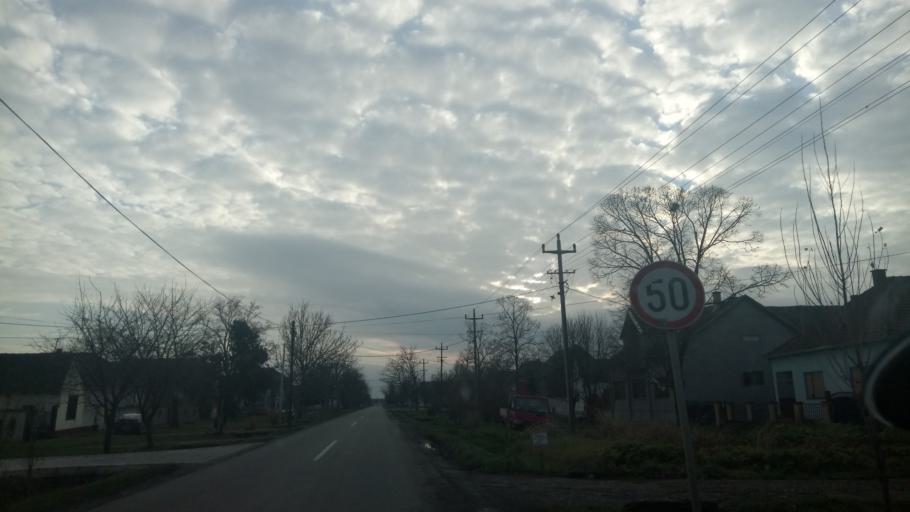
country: RS
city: Vojka
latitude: 44.9424
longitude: 20.1716
